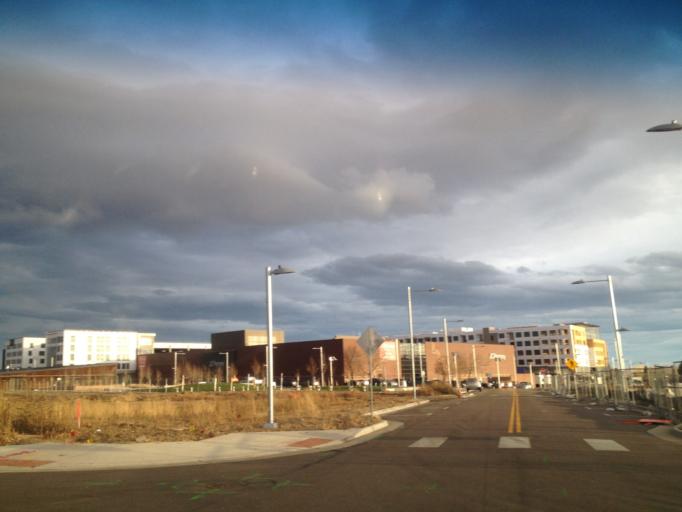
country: US
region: Colorado
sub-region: Adams County
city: Westminster
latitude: 39.8593
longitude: -105.0620
